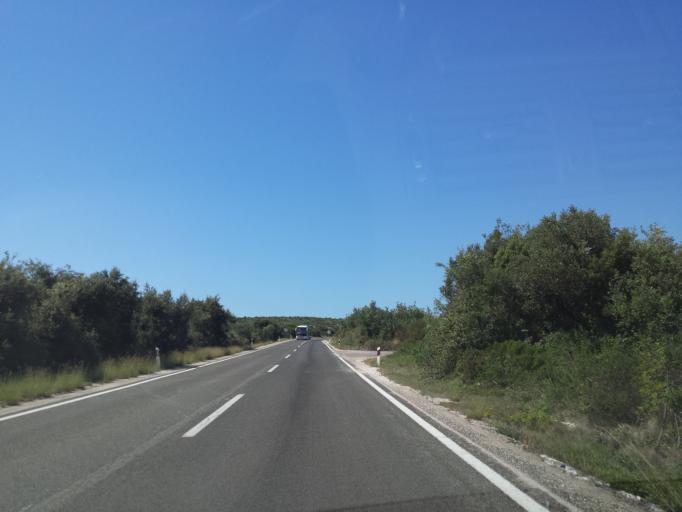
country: HR
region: Sibensko-Kniniska
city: Rogoznica
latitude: 43.5439
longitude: 15.9649
